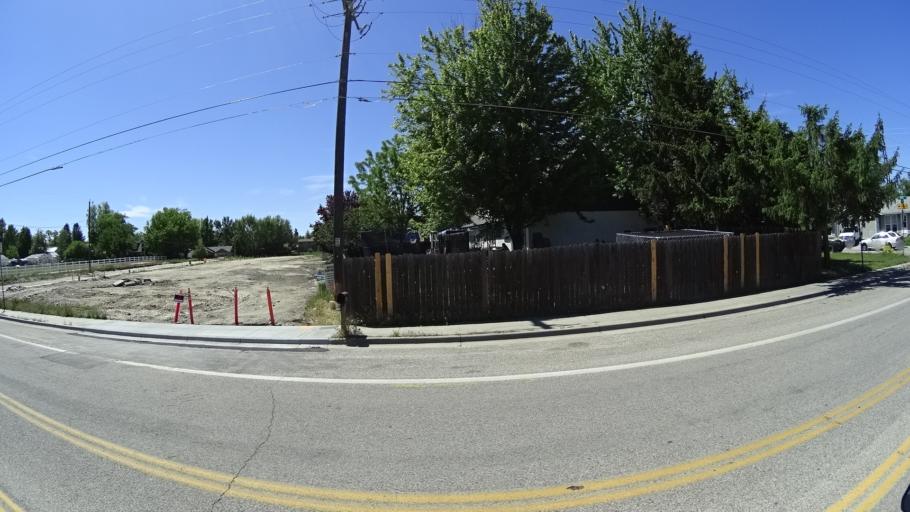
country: US
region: Idaho
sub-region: Ada County
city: Boise
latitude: 43.5734
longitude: -116.1573
